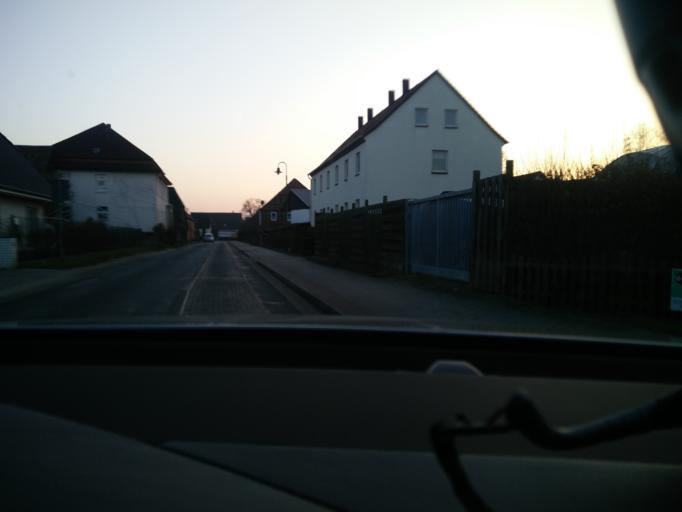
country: DE
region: Lower Saxony
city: Sehnde
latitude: 52.3183
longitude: 10.0255
